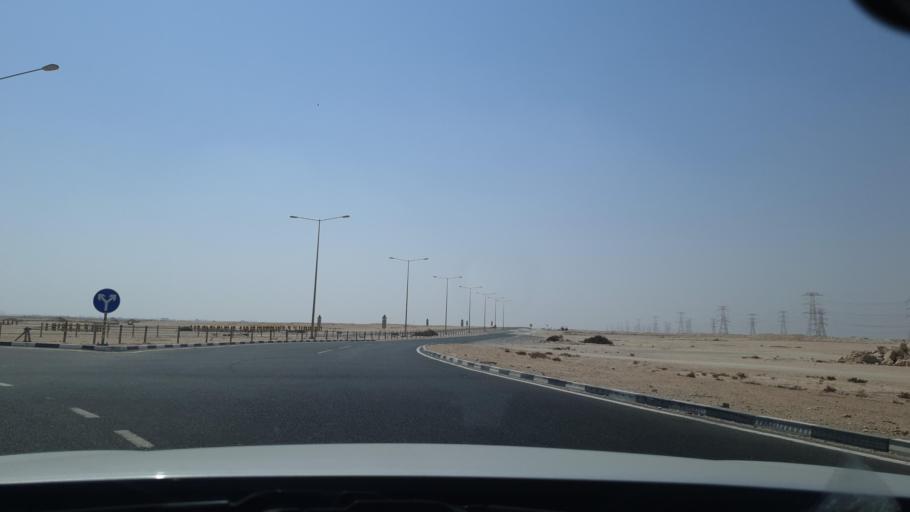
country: QA
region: Al Khawr
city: Al Khawr
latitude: 25.7316
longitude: 51.4572
